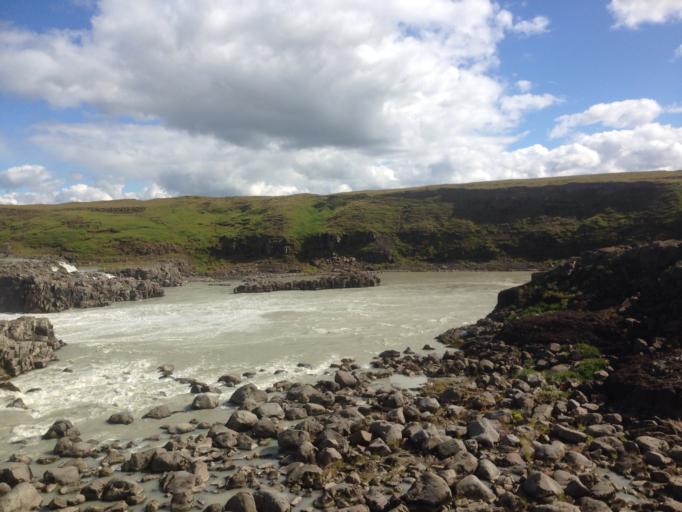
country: IS
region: South
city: Selfoss
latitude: 63.9238
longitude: -20.6735
